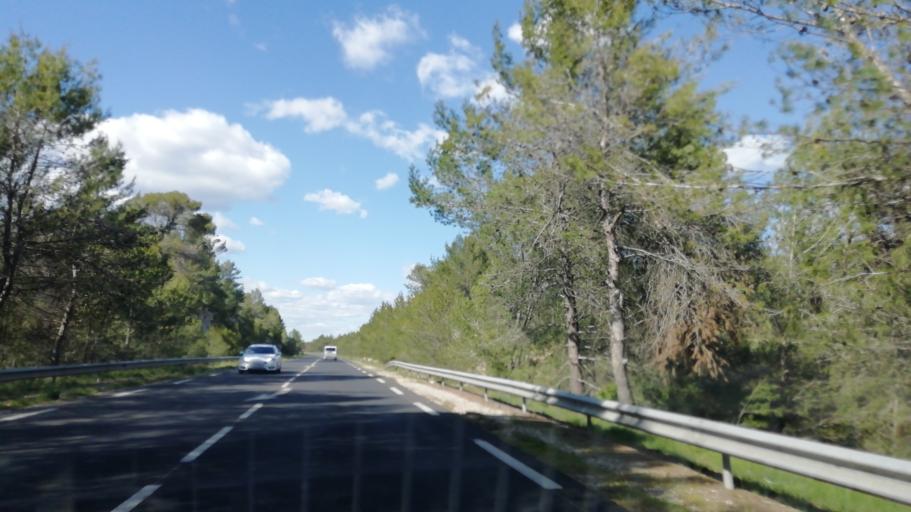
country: FR
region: Languedoc-Roussillon
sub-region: Departement de l'Herault
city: Saint-Clement-de-Riviere
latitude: 43.6895
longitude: 3.8241
